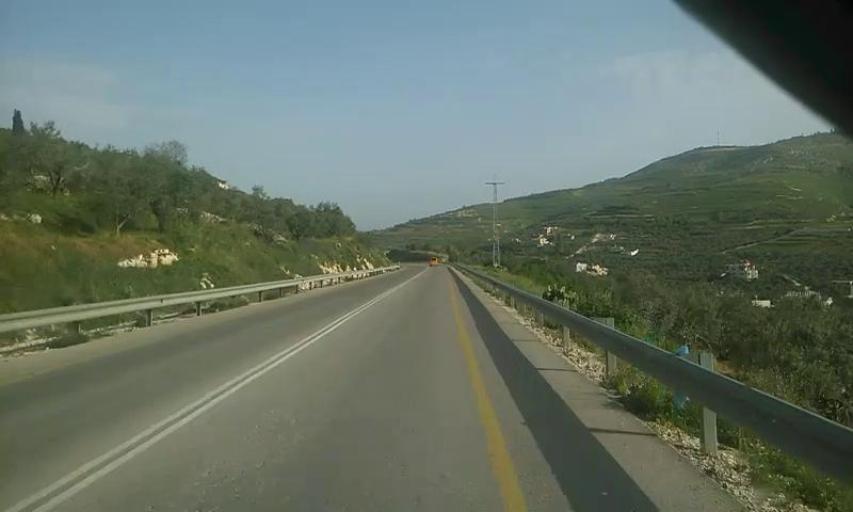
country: PS
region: West Bank
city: Madama
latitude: 32.1866
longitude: 35.2330
